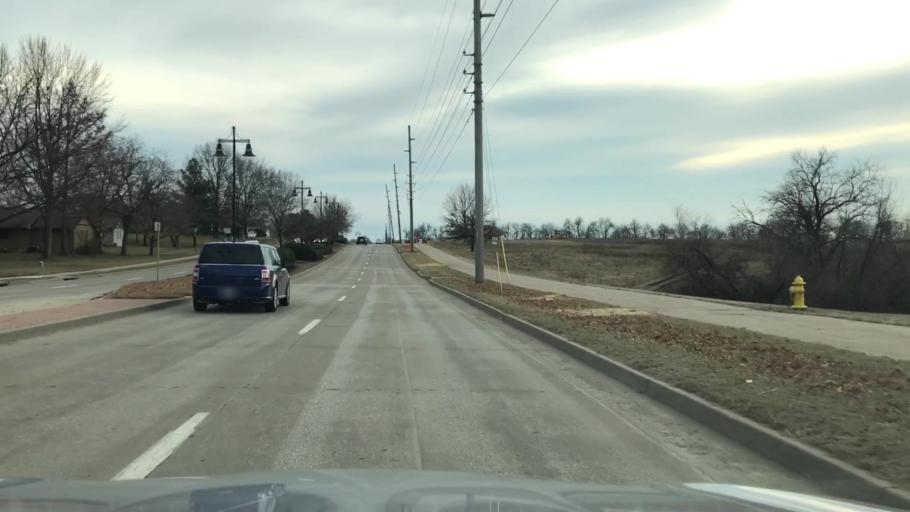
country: US
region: Missouri
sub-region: Jackson County
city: Lees Summit
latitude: 38.9195
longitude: -94.4132
